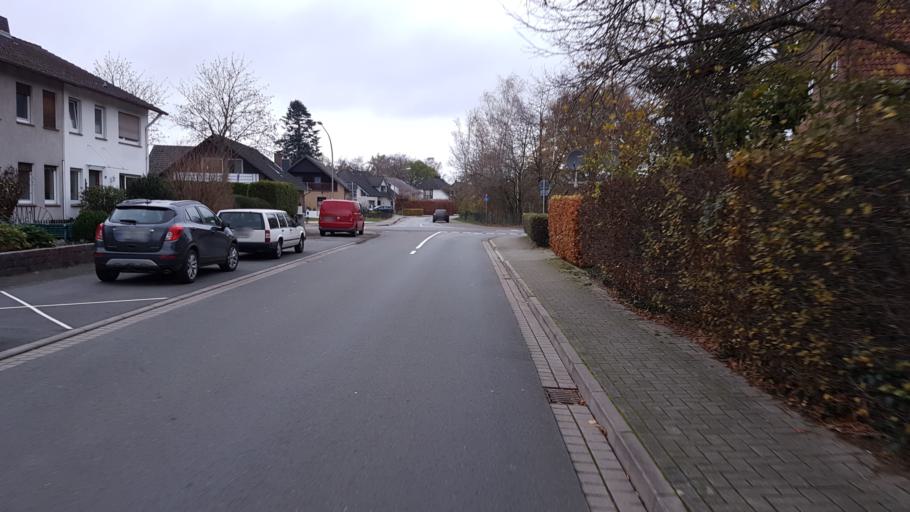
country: DE
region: North Rhine-Westphalia
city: Rahden
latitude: 52.4361
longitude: 8.6095
